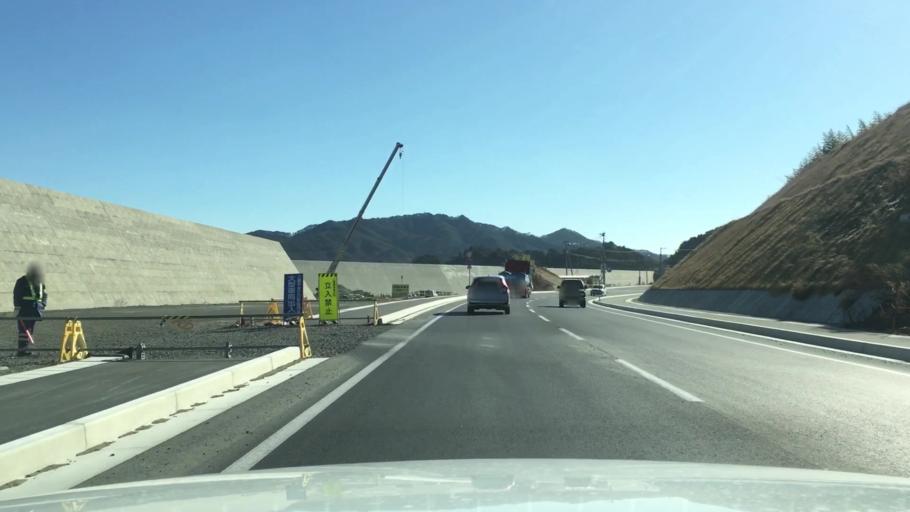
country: JP
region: Iwate
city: Yamada
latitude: 39.4552
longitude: 141.9593
